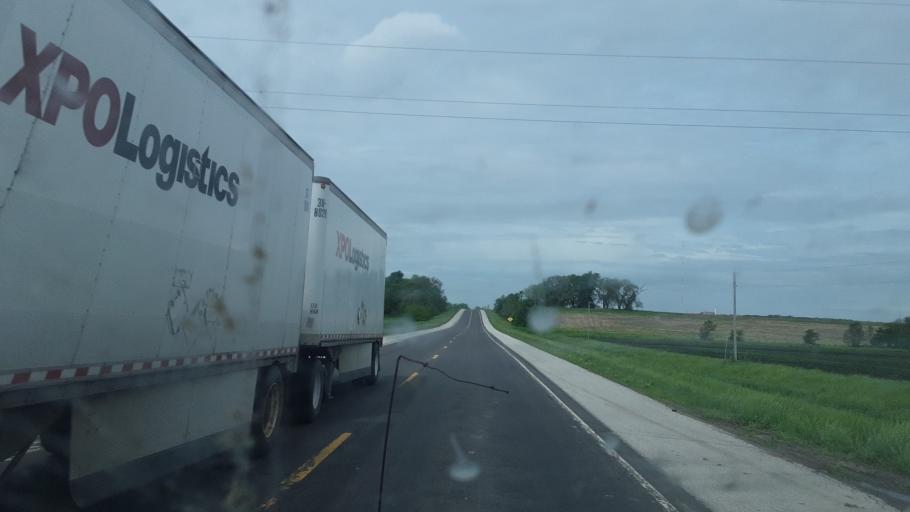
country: US
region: Illinois
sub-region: Hancock County
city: Warsaw
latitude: 40.3944
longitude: -91.5593
